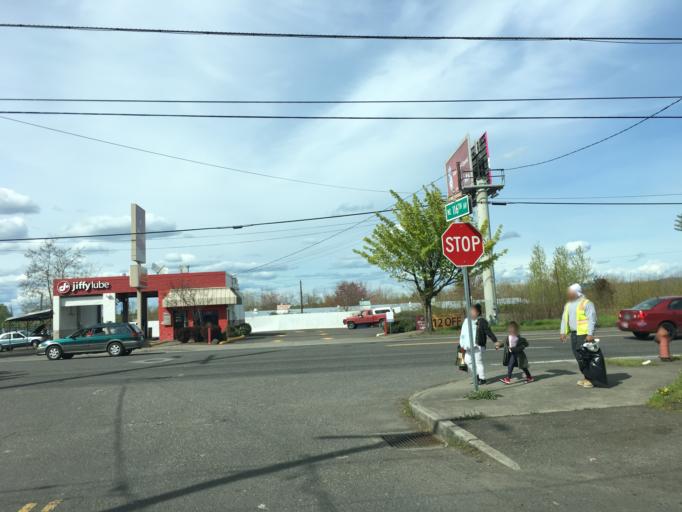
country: US
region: Oregon
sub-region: Multnomah County
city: Lents
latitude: 45.5576
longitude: -122.5431
